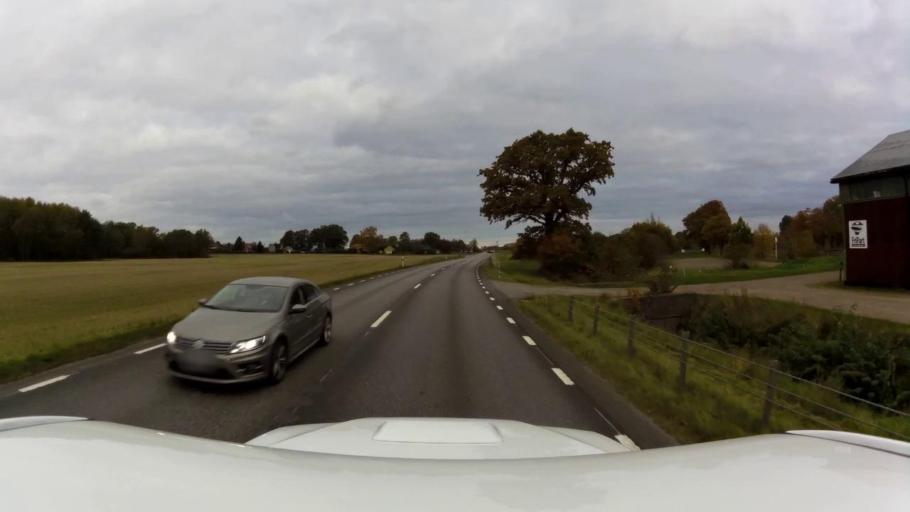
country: SE
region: OEstergoetland
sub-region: Linkopings Kommun
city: Ljungsbro
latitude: 58.5185
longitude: 15.4267
